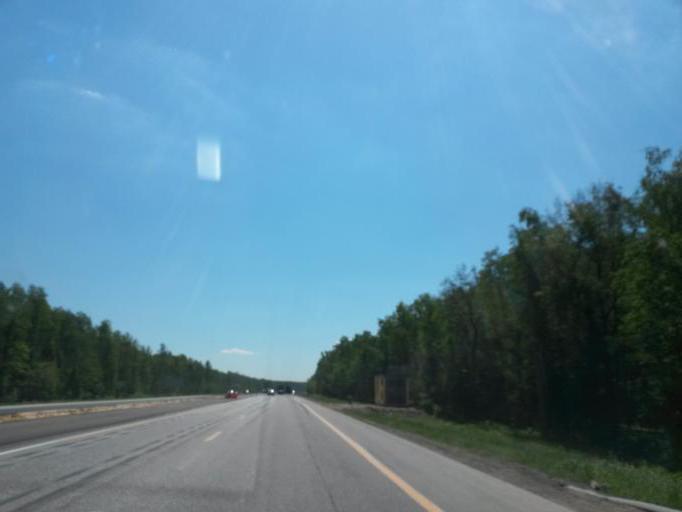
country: RU
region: Moskovskaya
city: Novyy Byt
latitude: 55.1175
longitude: 37.5756
